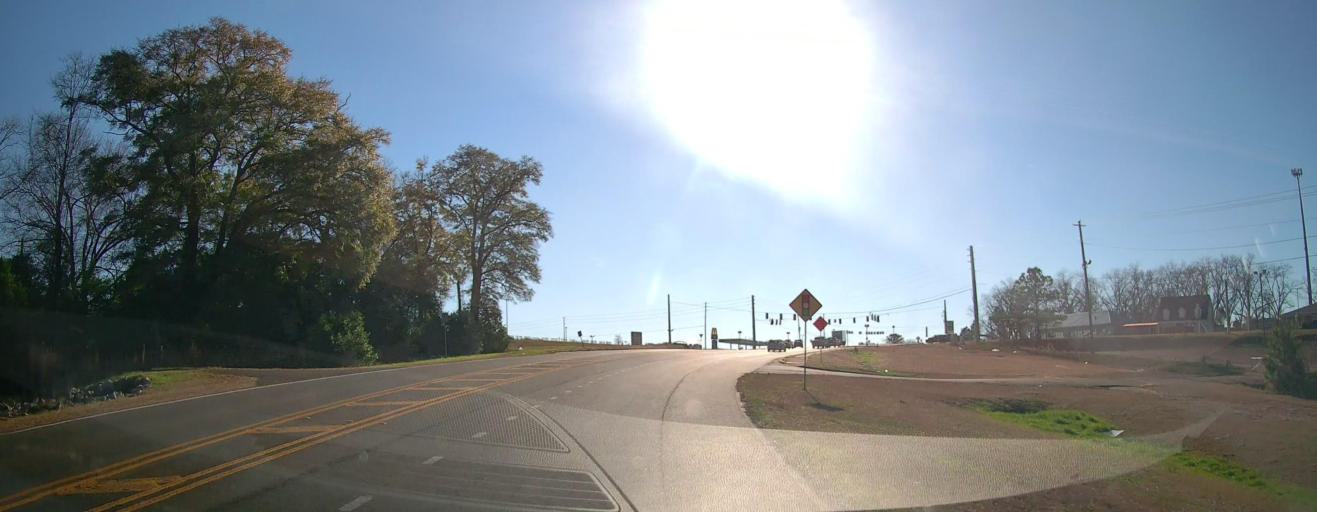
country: US
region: Georgia
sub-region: Sumter County
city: Americus
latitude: 32.0655
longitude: -84.2511
